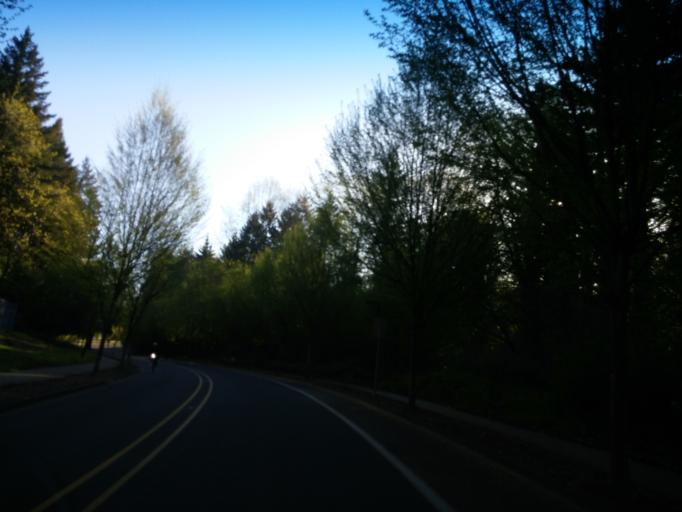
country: US
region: Oregon
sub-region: Washington County
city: Cedar Hills
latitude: 45.5076
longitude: -122.7878
